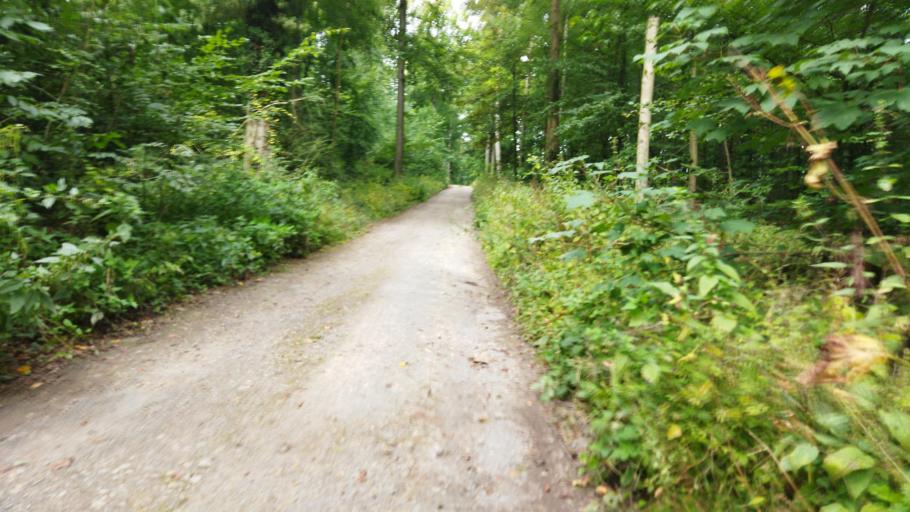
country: DE
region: Lower Saxony
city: Hilter
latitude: 52.1218
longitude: 8.1518
